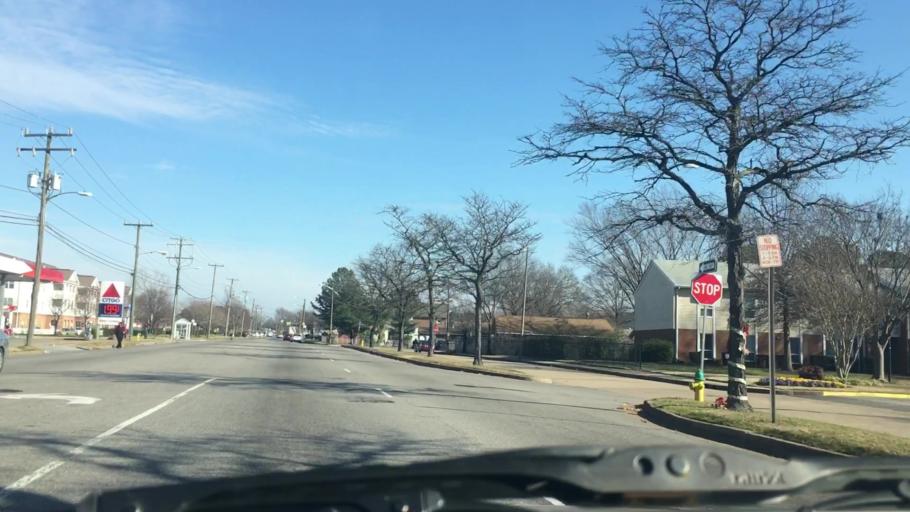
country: US
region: Virginia
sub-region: City of Norfolk
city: Norfolk
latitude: 36.8541
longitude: -76.2628
